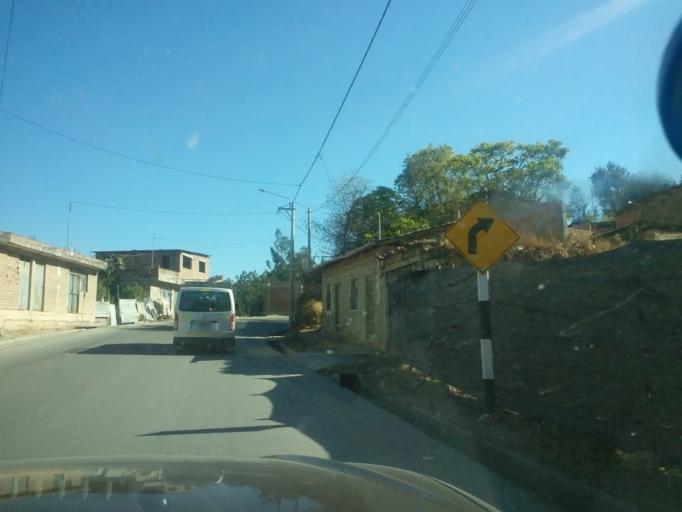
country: PE
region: Apurimac
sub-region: Provincia de Andahuaylas
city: San Jeronimo
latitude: -13.6496
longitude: -73.3702
